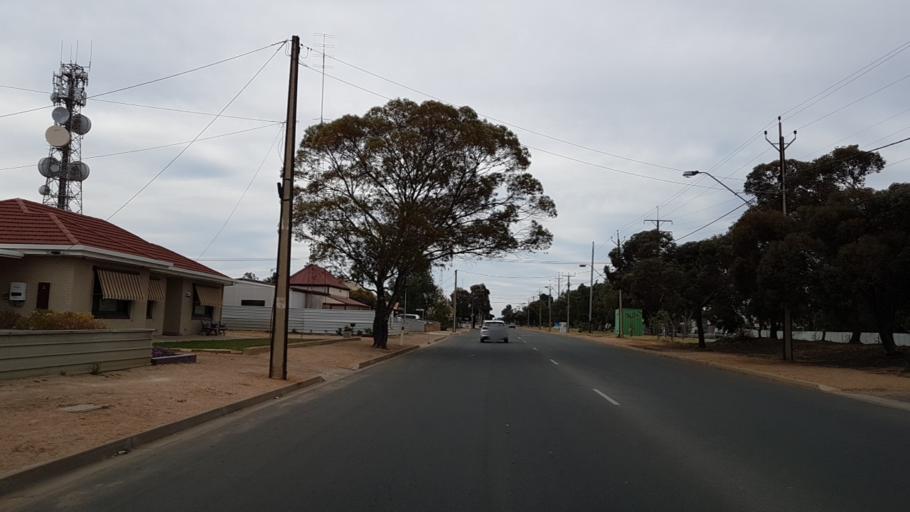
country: AU
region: South Australia
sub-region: Port Pirie City and Dists
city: Port Pirie
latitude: -33.1871
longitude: 138.0038
